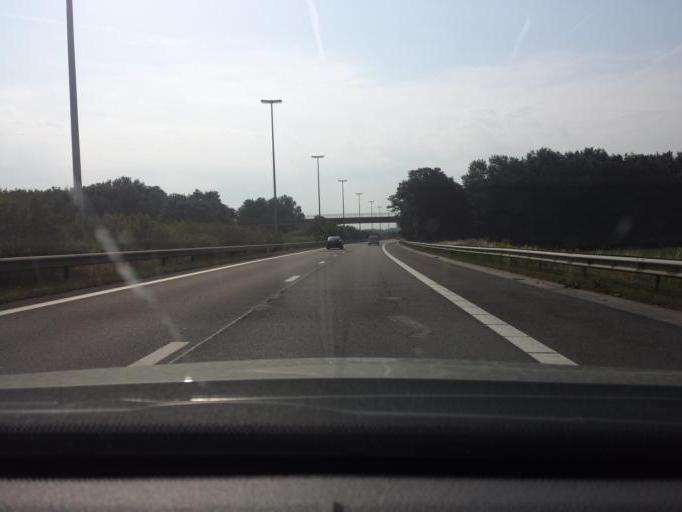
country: BE
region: Flanders
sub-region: Provincie Limburg
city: Diepenbeek
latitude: 50.8889
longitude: 5.4381
